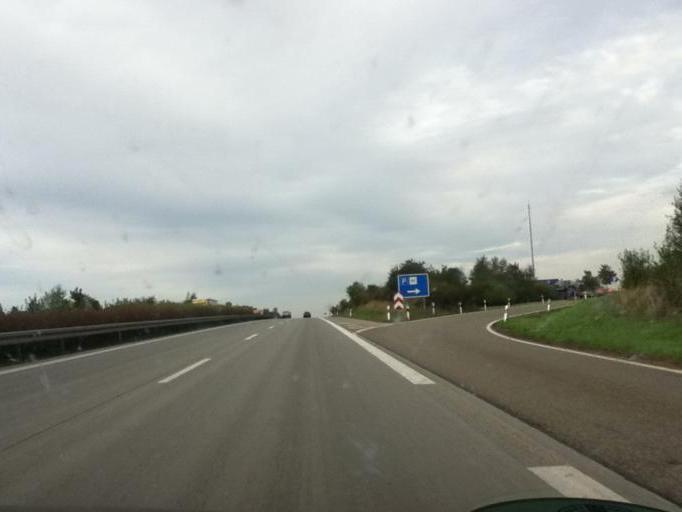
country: DE
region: Saxony
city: Neukirchen
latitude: 50.7793
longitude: 12.8234
